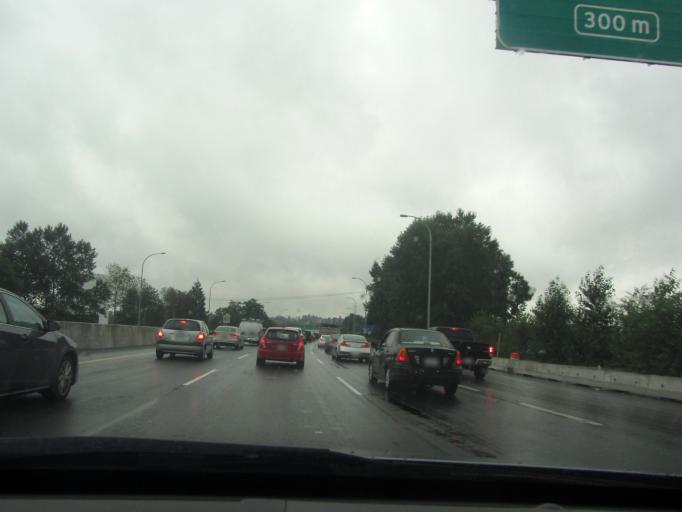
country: CA
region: British Columbia
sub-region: Fraser Valley Regional District
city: North Vancouver
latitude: 49.2666
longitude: -123.0264
